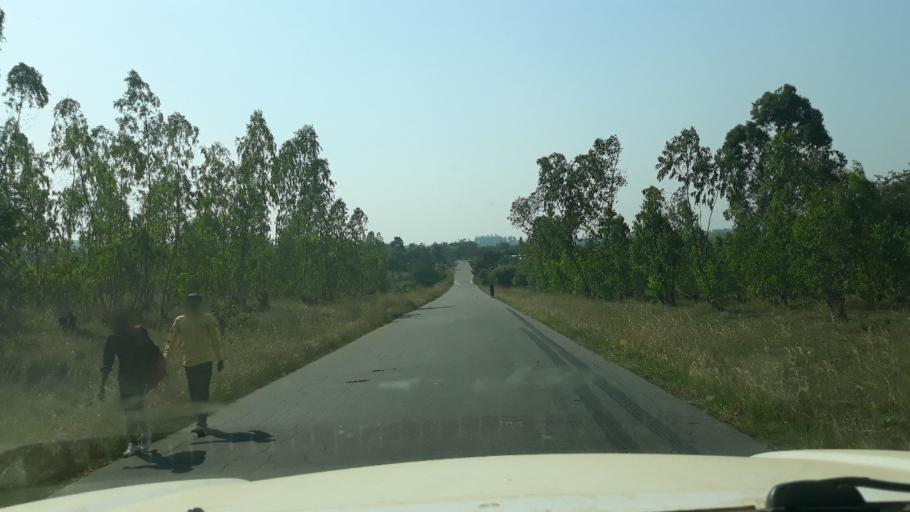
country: CD
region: South Kivu
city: Uvira
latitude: -3.1903
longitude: 29.1535
